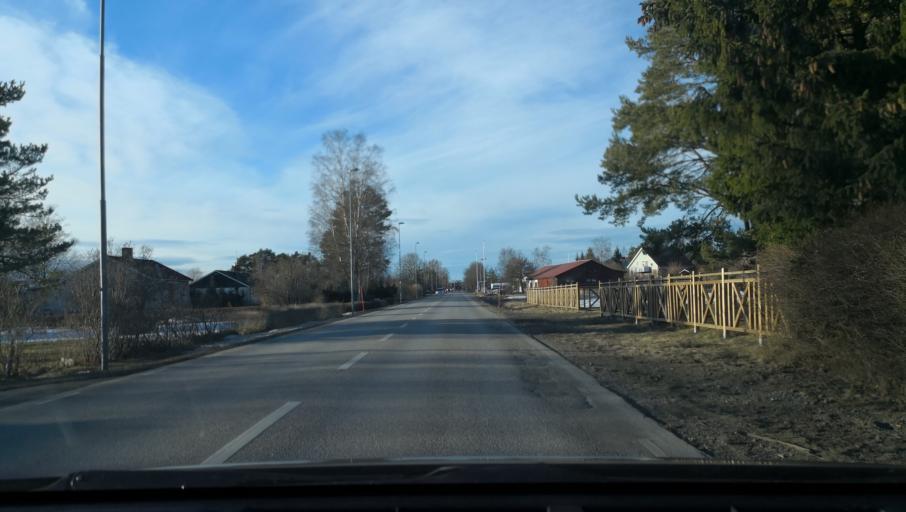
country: SE
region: Uppsala
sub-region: Osthammars Kommun
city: OEsthammar
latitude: 60.2826
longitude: 18.2940
